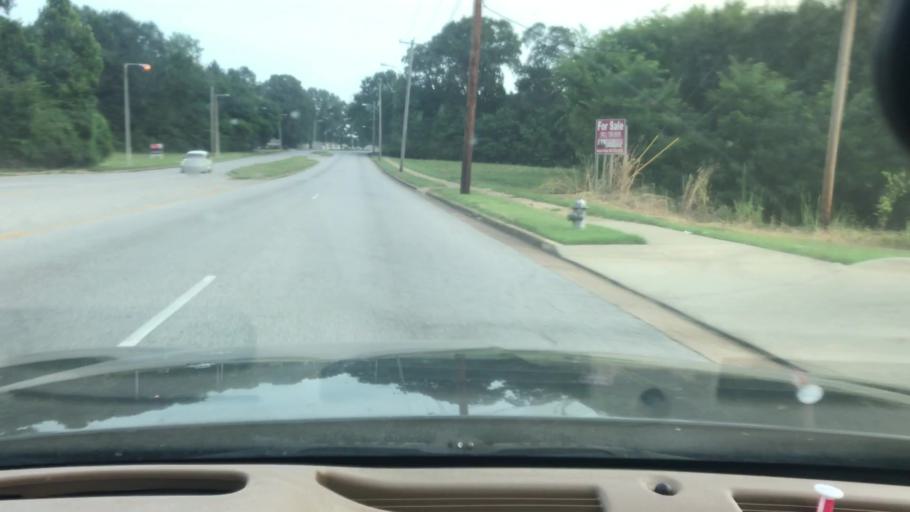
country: US
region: Tennessee
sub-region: Shelby County
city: Bartlett
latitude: 35.1739
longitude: -89.8698
